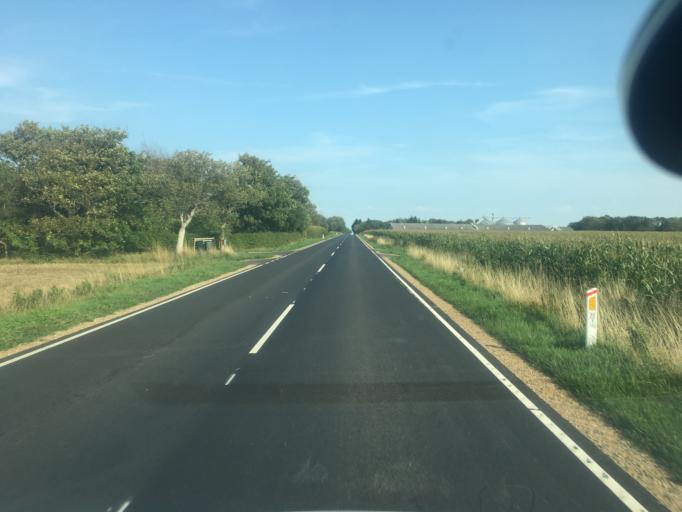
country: DK
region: South Denmark
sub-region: Tonder Kommune
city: Logumkloster
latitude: 55.0006
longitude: 8.9175
